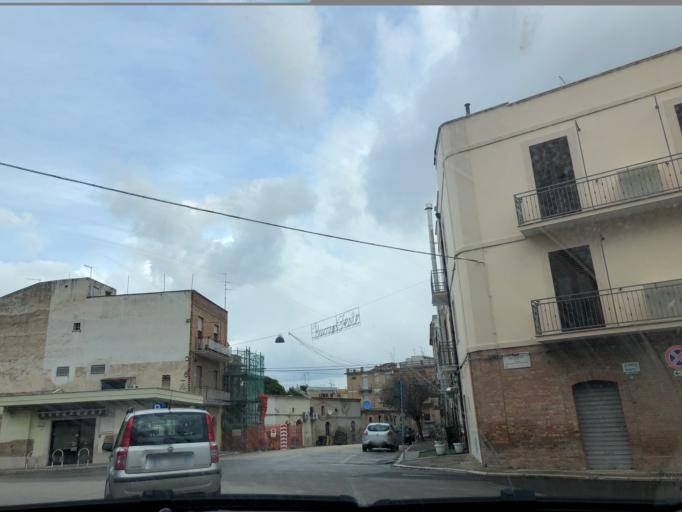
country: IT
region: Apulia
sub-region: Provincia di Foggia
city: Lucera
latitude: 41.5106
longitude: 15.3316
